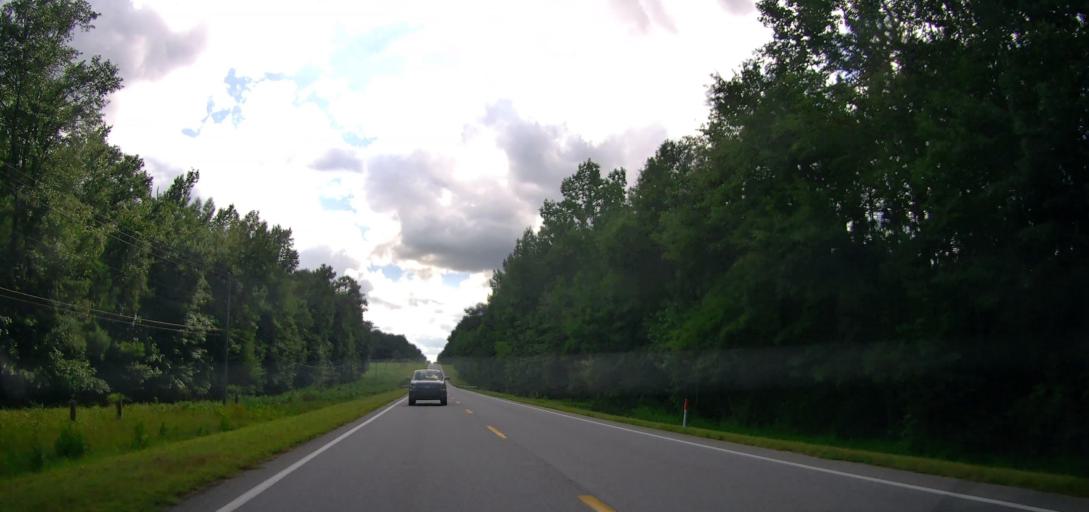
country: US
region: Alabama
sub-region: Russell County
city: Ladonia
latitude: 32.4612
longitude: -85.1720
